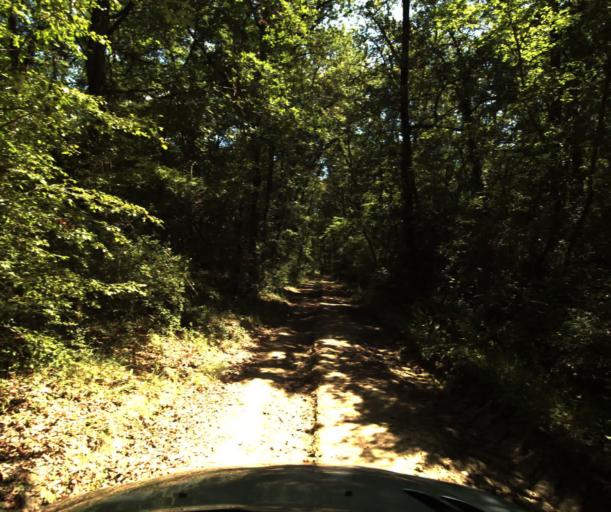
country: FR
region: Midi-Pyrenees
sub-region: Departement de la Haute-Garonne
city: Labastidette
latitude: 43.4630
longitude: 1.2269
